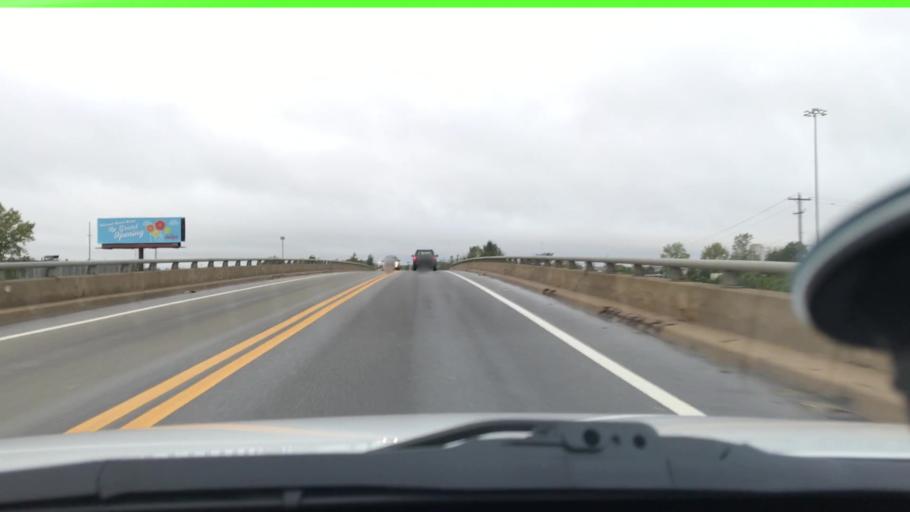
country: US
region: Ohio
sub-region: Franklin County
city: Lincoln Village
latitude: 39.9835
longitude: -83.1287
